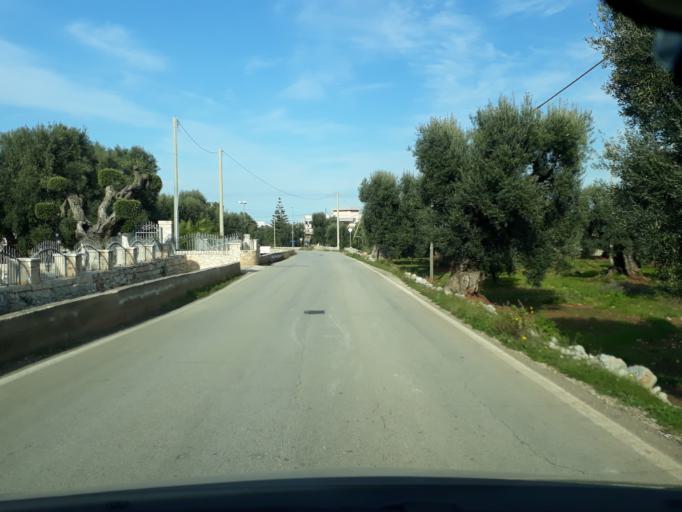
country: IT
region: Apulia
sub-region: Provincia di Brindisi
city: Fasano
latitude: 40.8226
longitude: 17.3594
